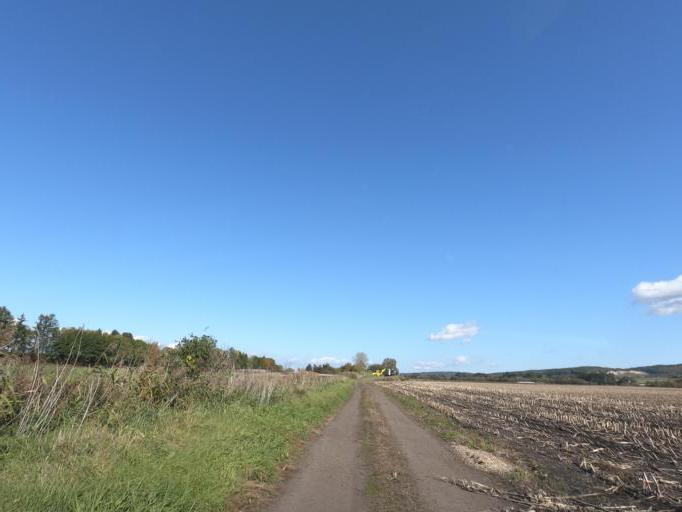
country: JP
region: Hokkaido
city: Otofuke
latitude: 43.0627
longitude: 143.2782
